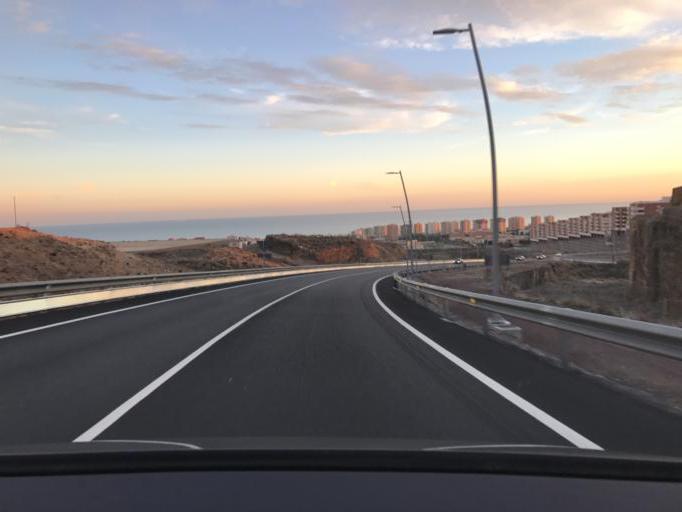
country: ES
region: Andalusia
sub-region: Provincia de Almeria
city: Aguadulce
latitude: 36.8250
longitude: -2.5822
